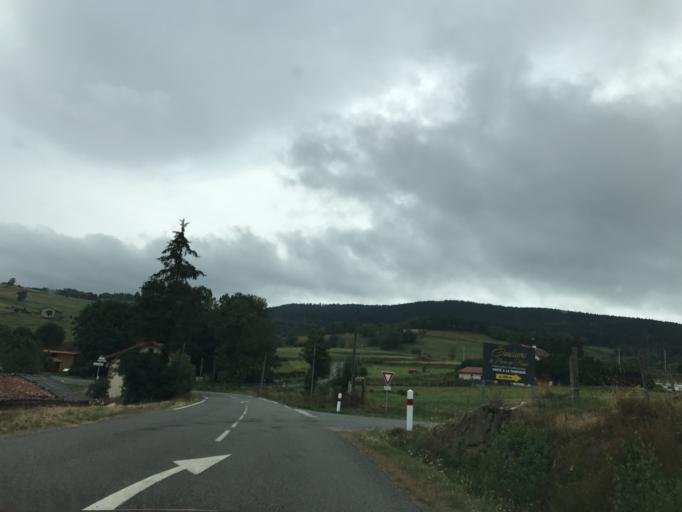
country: FR
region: Rhone-Alpes
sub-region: Departement de la Loire
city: Sail-sous-Couzan
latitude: 45.6791
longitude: 3.8892
